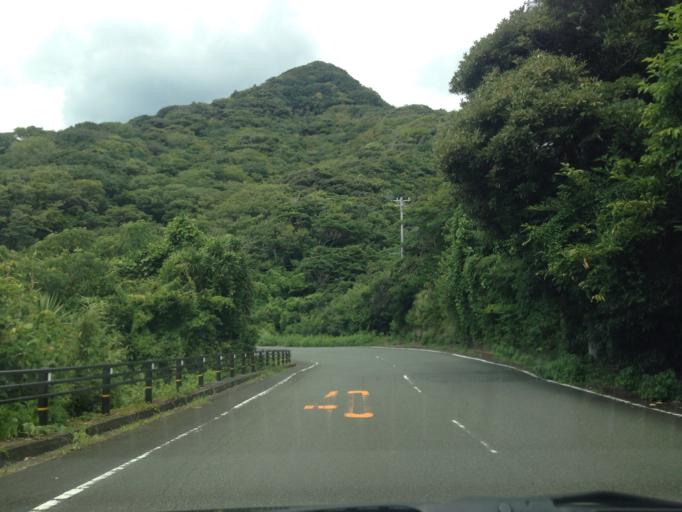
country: JP
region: Shizuoka
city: Shimoda
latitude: 34.6680
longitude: 138.7914
